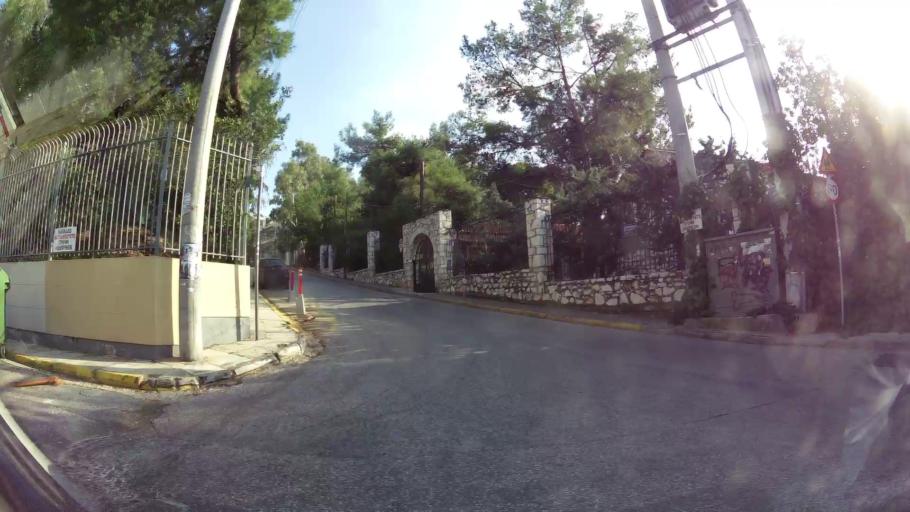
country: GR
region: Attica
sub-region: Nomarchia Athinas
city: Agia Paraskevi
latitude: 38.0099
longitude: 23.8344
